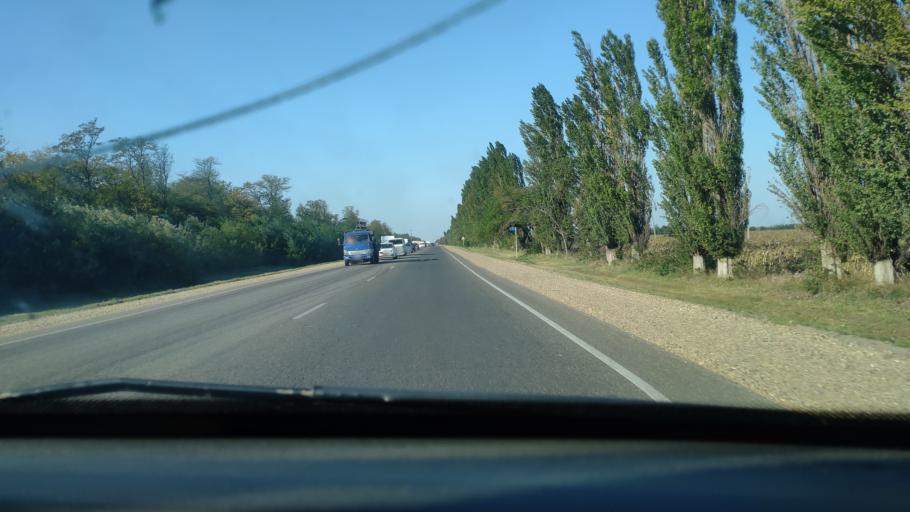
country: RU
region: Krasnodarskiy
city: Novotitarovskaya
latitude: 45.2705
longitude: 39.0042
